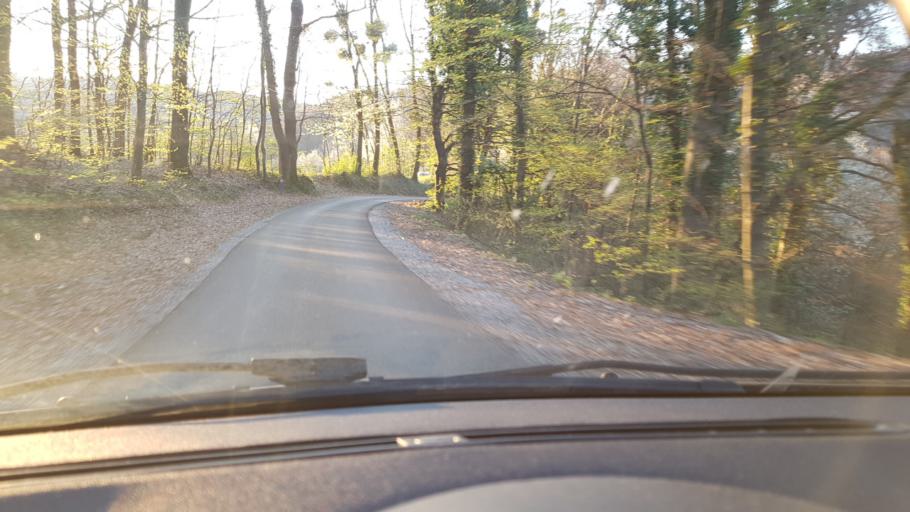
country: HR
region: Krapinsko-Zagorska
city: Pregrada
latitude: 46.1692
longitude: 15.6920
